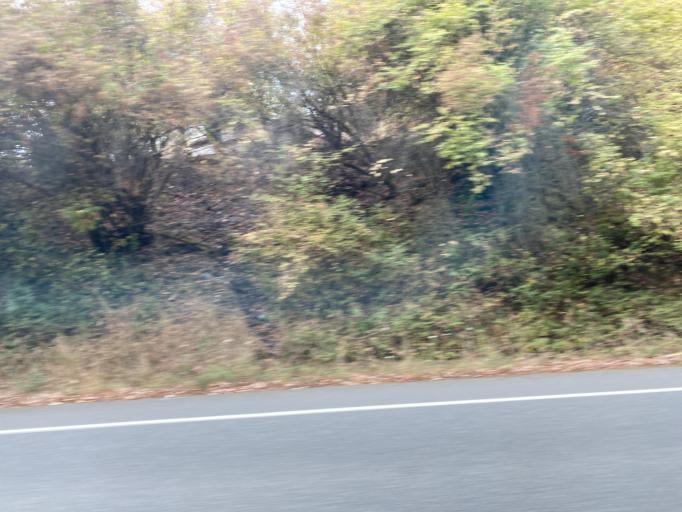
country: US
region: Washington
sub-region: Island County
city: Coupeville
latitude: 48.2133
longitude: -122.7215
